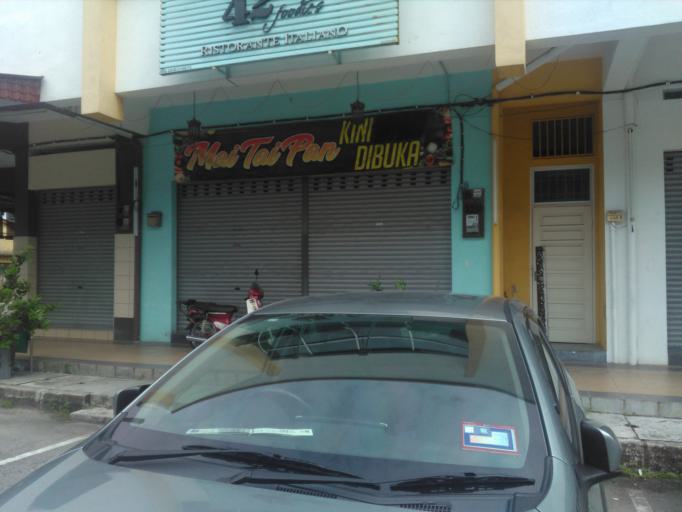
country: MY
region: Perak
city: Ipoh
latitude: 4.6096
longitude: 101.0996
